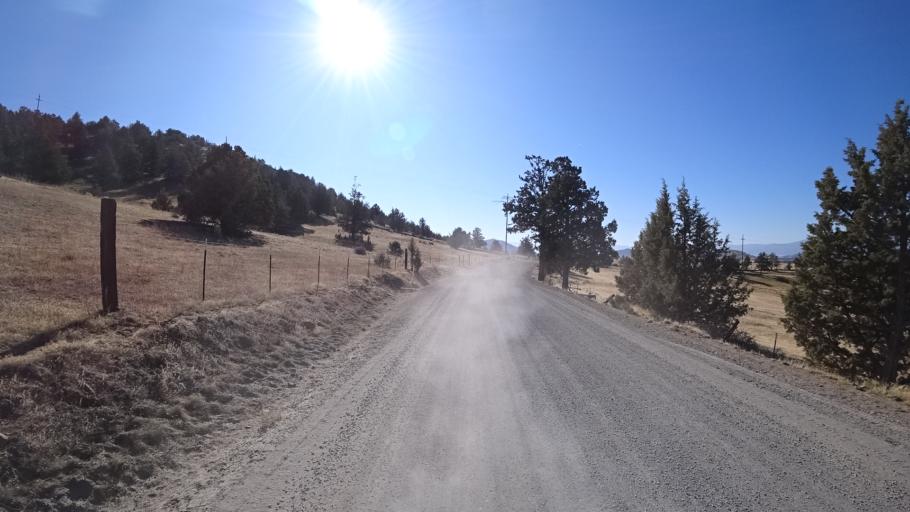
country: US
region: California
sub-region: Siskiyou County
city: Montague
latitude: 41.7123
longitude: -122.3760
